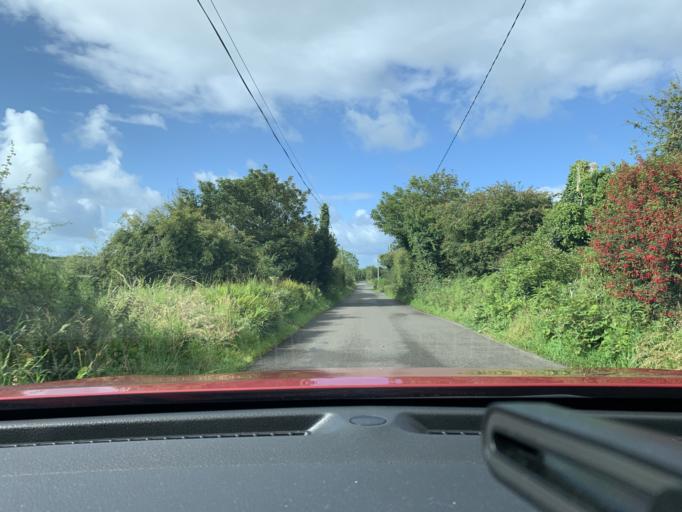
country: IE
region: Connaught
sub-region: Sligo
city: Strandhill
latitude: 54.3652
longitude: -8.6015
